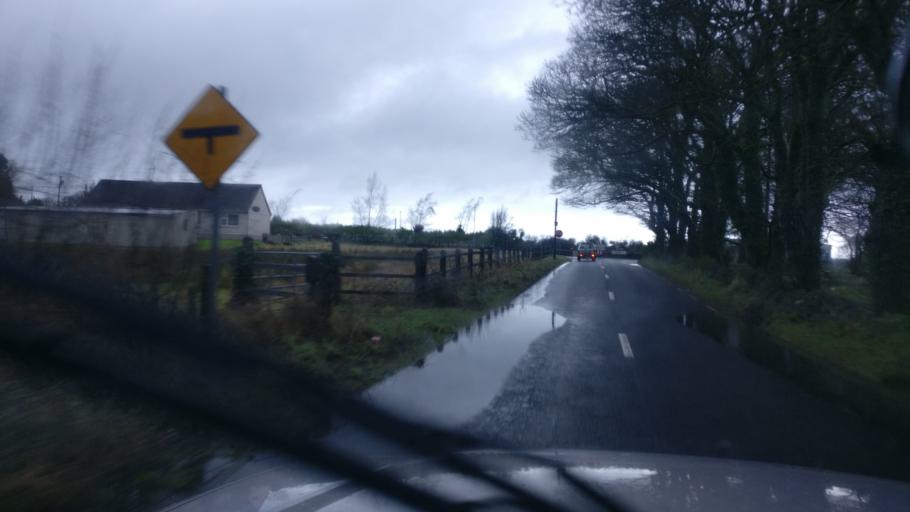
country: IE
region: Connaught
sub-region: County Galway
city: Ballinasloe
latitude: 53.3273
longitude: -8.4067
